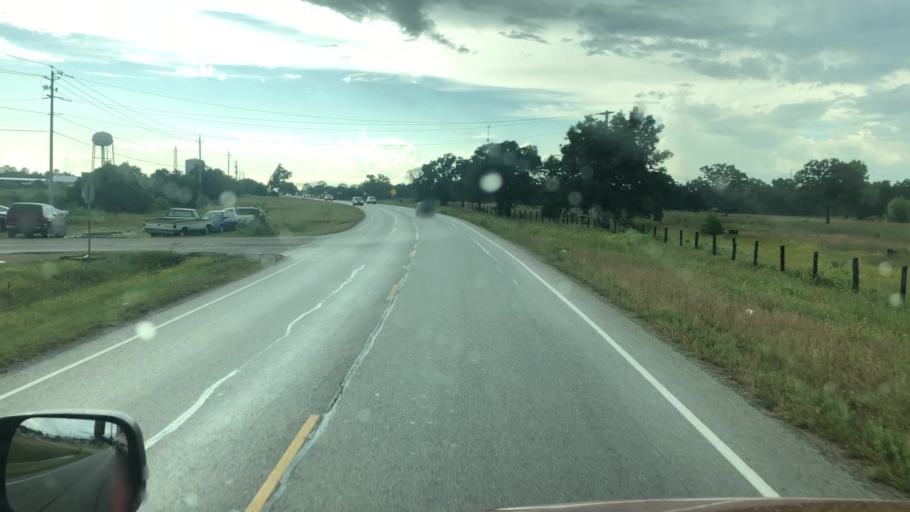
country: US
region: Texas
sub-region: Bastrop County
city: Bastrop
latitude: 30.1077
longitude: -97.2883
